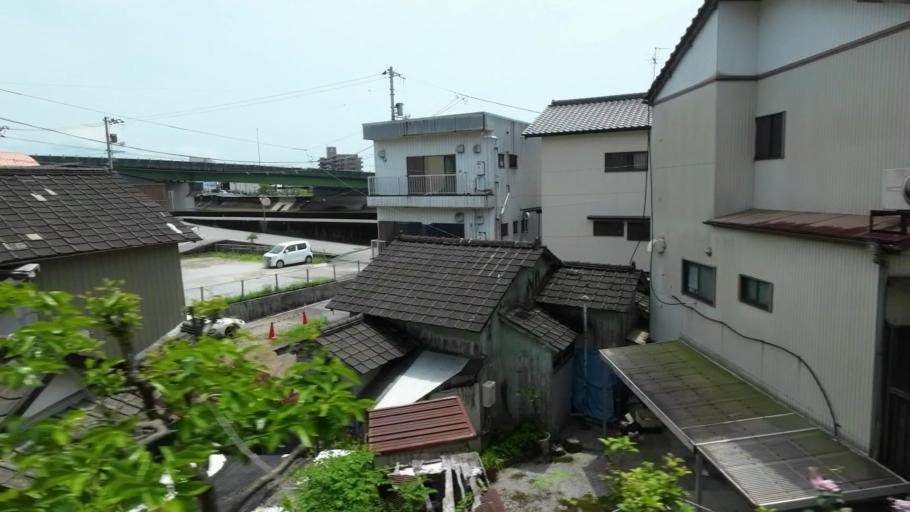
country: JP
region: Kochi
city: Kochi-shi
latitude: 33.5746
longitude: 133.5546
